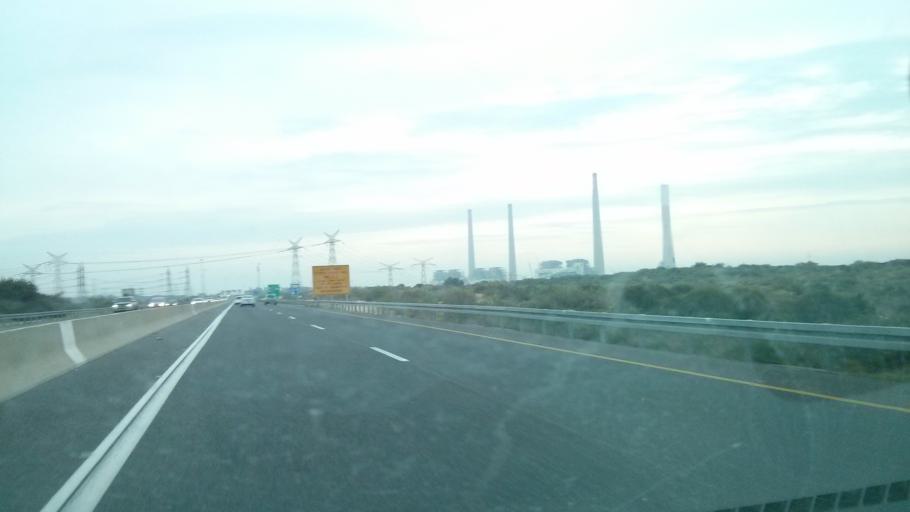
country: IL
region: Haifa
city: Hadera
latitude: 32.4801
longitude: 34.9081
